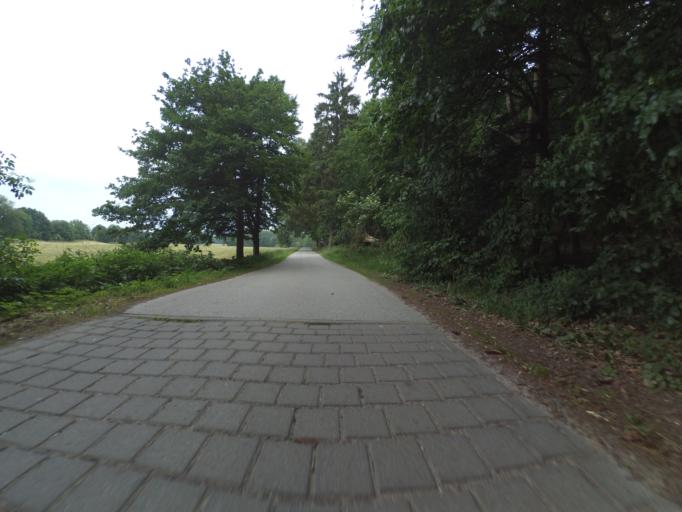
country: DE
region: Mecklenburg-Vorpommern
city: Lubz
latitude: 53.4125
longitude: 12.1346
